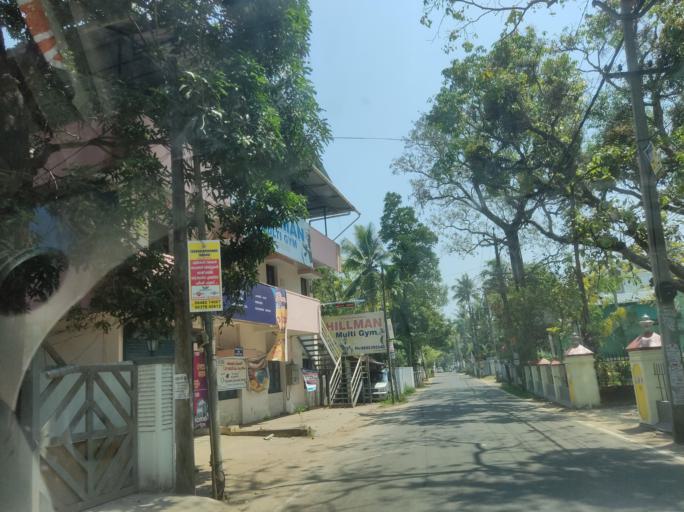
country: IN
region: Kerala
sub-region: Alappuzha
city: Arukutti
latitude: 9.8567
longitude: 76.2932
